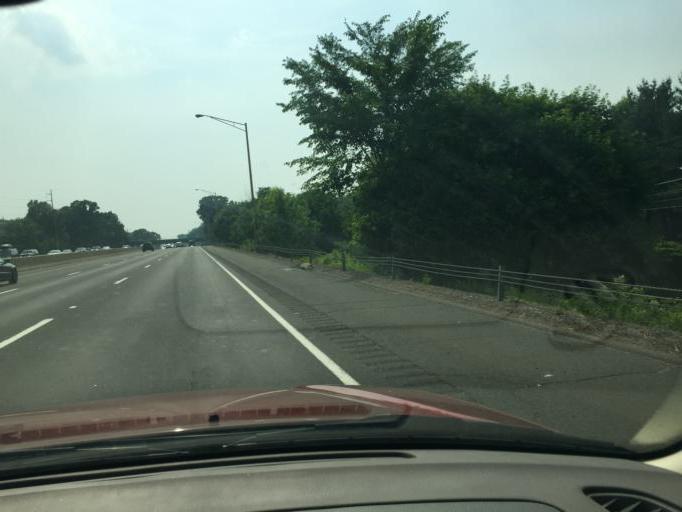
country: US
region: Connecticut
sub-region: Fairfield County
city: Westport
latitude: 41.1229
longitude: -73.3496
